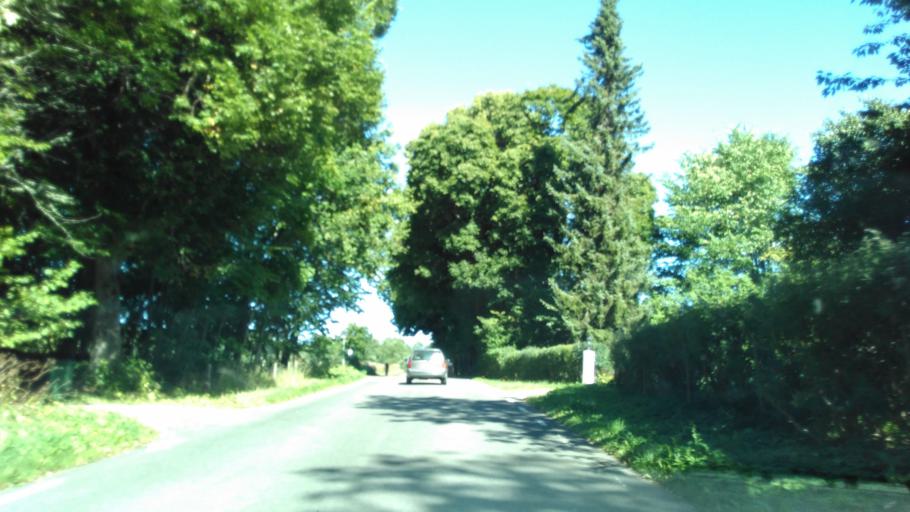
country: SE
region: Vaestra Goetaland
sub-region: Skara Kommun
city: Axvall
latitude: 58.4391
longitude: 13.6532
